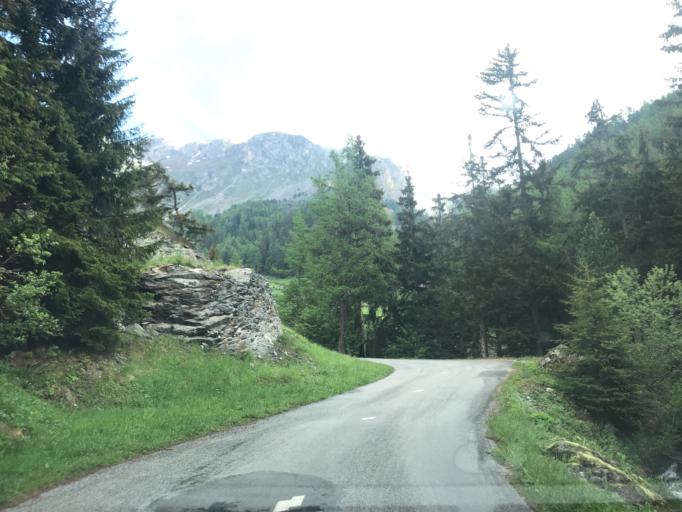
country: FR
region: Rhone-Alpes
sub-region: Departement de la Savoie
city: Modane
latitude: 45.2235
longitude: 6.6512
